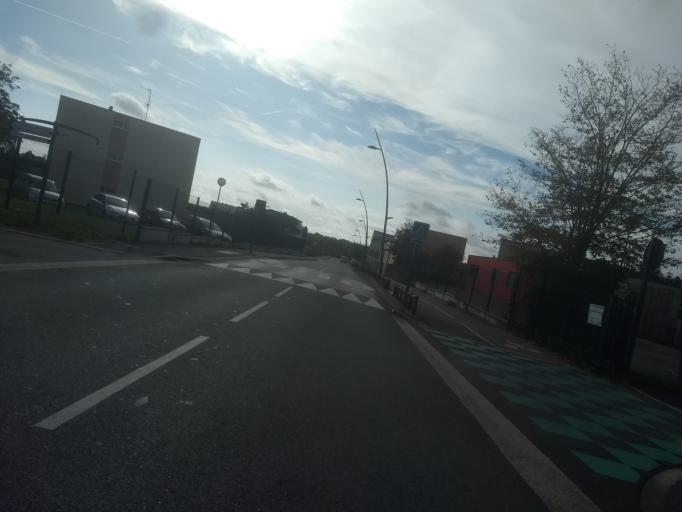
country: FR
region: Nord-Pas-de-Calais
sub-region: Departement du Pas-de-Calais
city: Dainville
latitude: 50.2912
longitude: 2.7355
